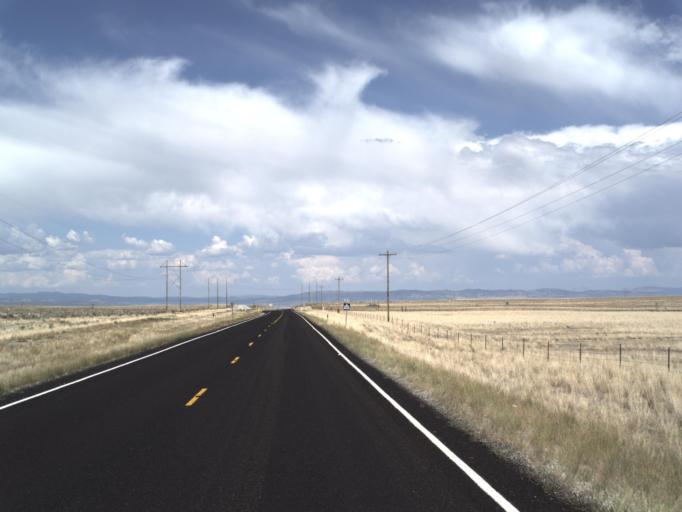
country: US
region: Idaho
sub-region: Power County
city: American Falls
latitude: 41.9661
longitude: -113.0680
